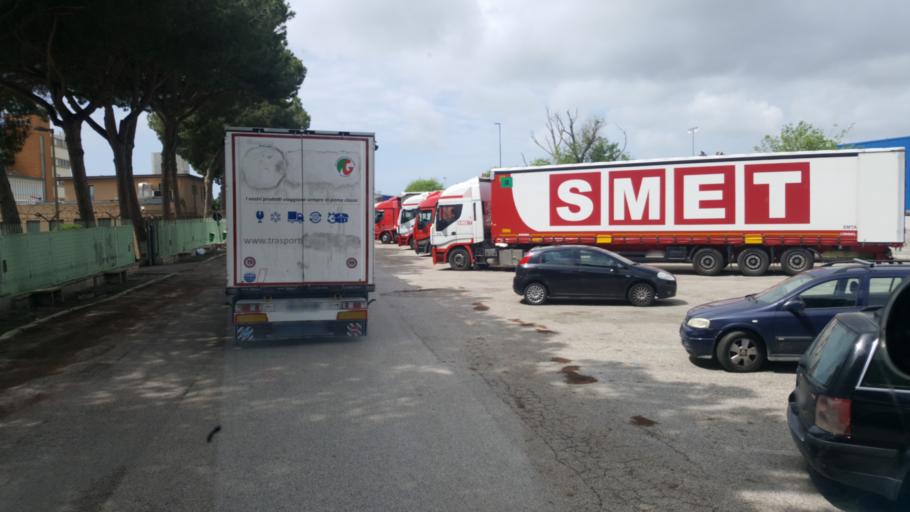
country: IT
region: Latium
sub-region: Citta metropolitana di Roma Capitale
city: Anzio
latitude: 41.5134
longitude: 12.6289
